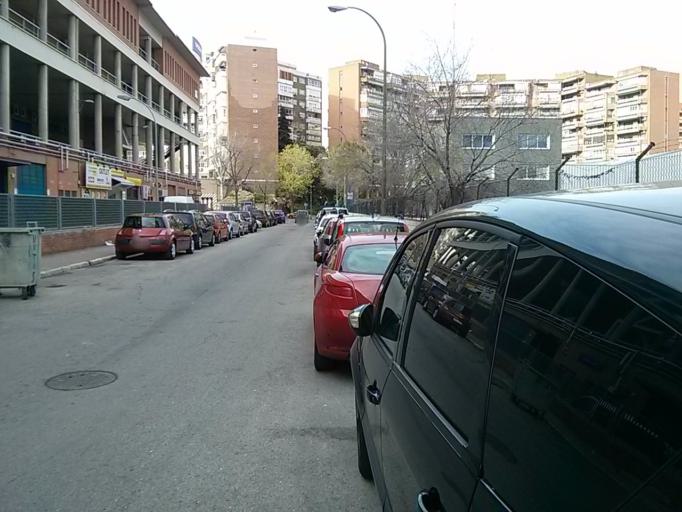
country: ES
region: Madrid
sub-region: Provincia de Madrid
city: Pinar de Chamartin
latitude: 40.4874
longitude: -3.6674
